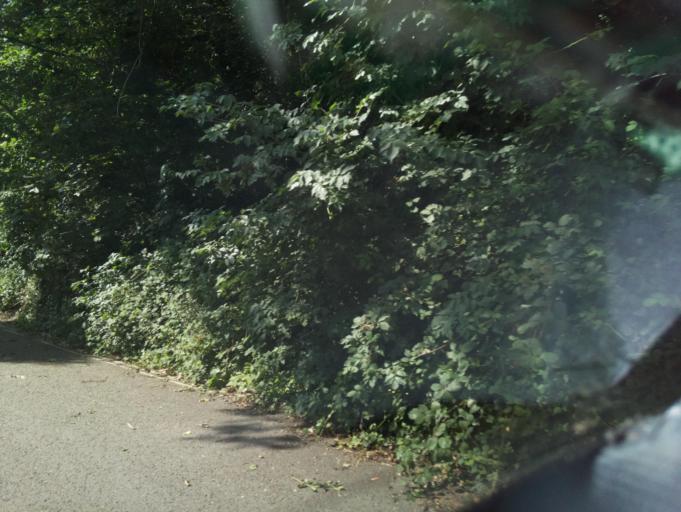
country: GB
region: England
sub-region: Devon
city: Dartmouth
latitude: 50.3540
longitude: -3.5637
